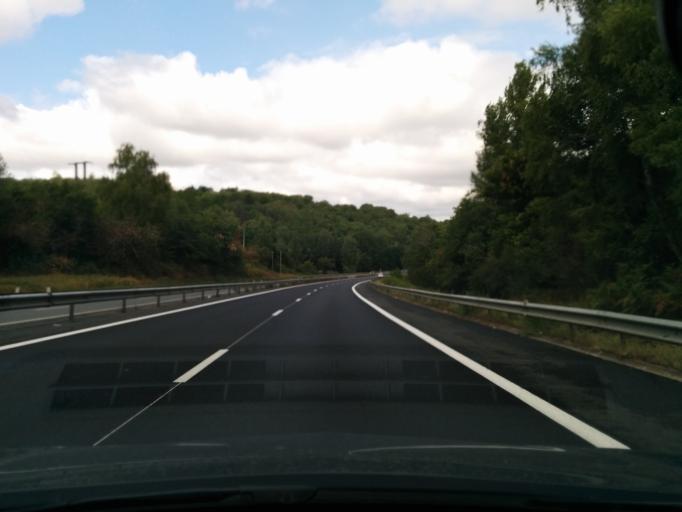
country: FR
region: Limousin
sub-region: Departement de la Correze
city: Brive-la-Gaillarde
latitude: 45.1256
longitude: 1.4951
